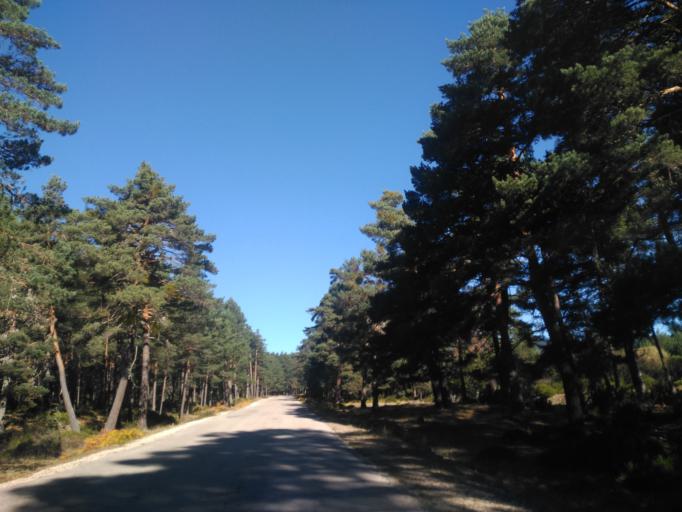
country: ES
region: Castille and Leon
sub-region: Provincia de Soria
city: Vinuesa
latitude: 41.9904
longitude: -2.7995
